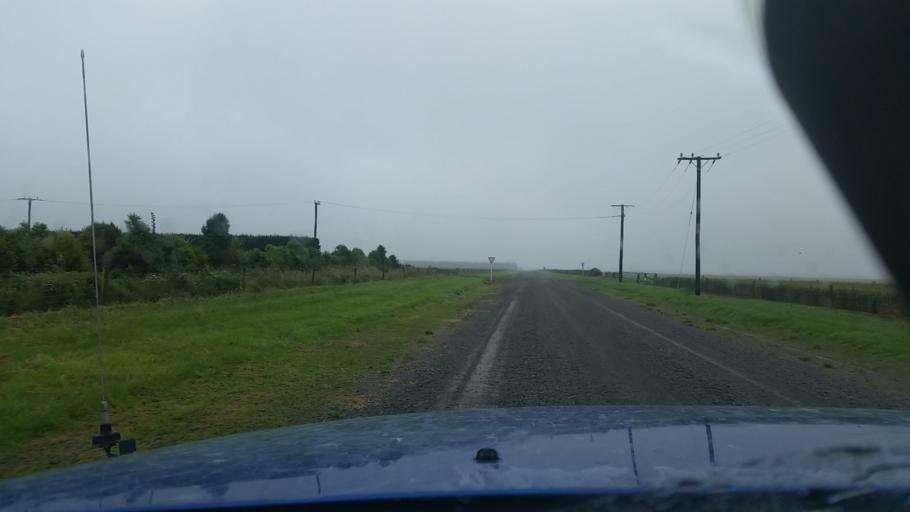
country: NZ
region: Canterbury
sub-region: Ashburton District
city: Rakaia
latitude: -43.7090
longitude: 171.8922
